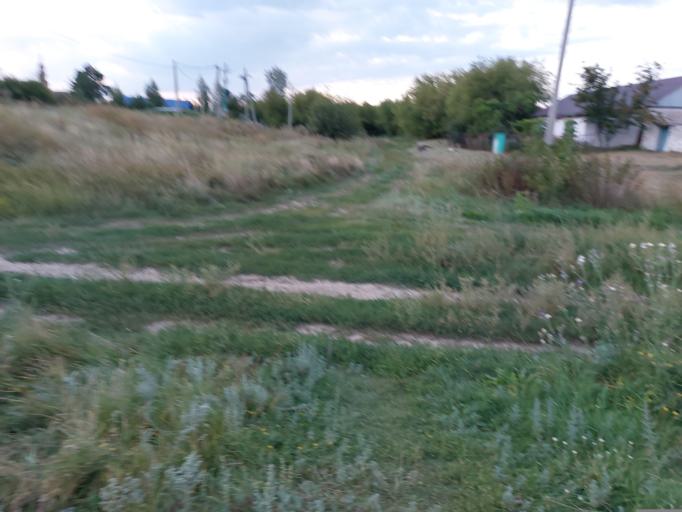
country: RU
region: Lipetsk
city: Dolgorukovo
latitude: 52.3753
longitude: 38.0578
